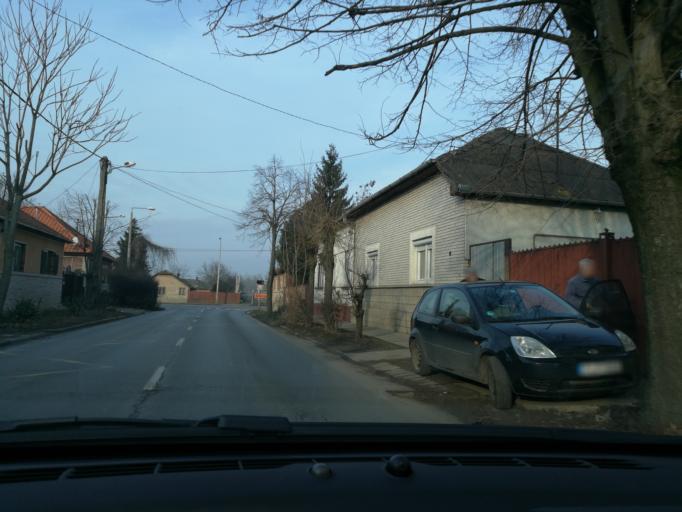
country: HU
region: Szabolcs-Szatmar-Bereg
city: Nyiregyhaza
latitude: 47.9564
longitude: 21.6940
